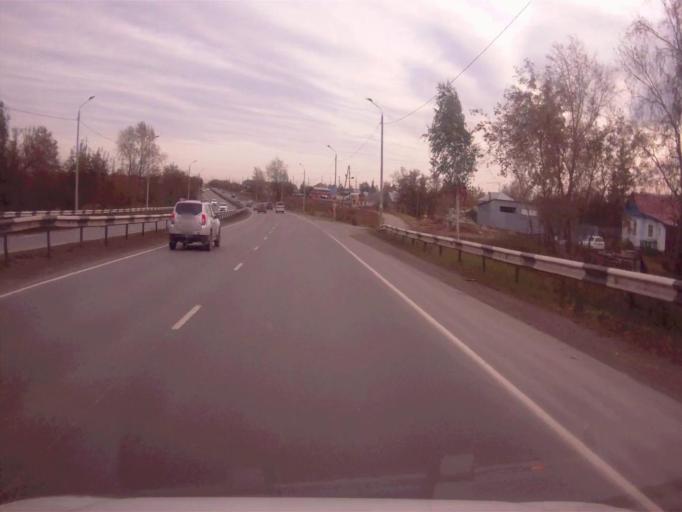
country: RU
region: Chelyabinsk
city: Novosineglazovskiy
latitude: 55.0476
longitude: 61.4161
